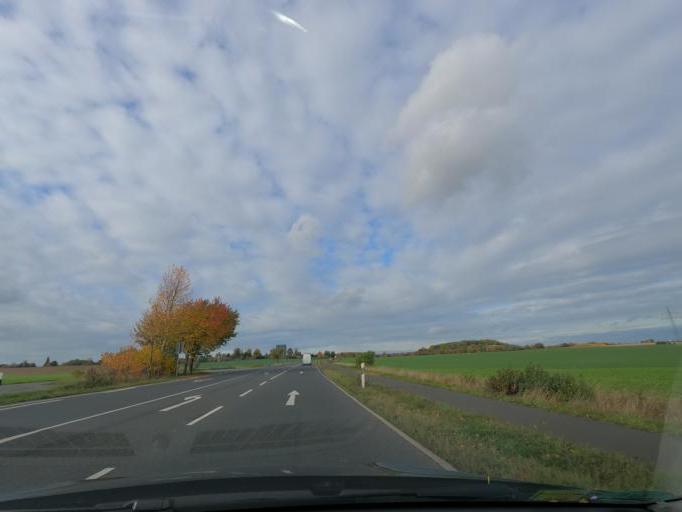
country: DE
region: Lower Saxony
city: Leiferde
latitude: 52.1787
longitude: 10.5050
